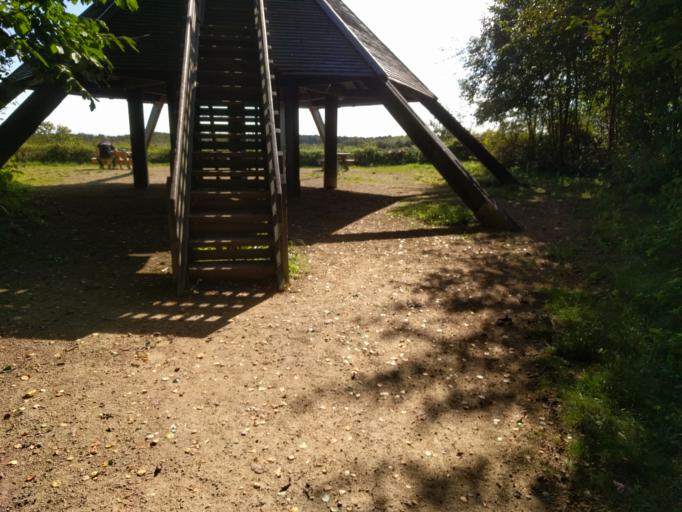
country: GB
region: England
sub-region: Warrington
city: Culcheth
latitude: 53.4246
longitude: -2.5025
